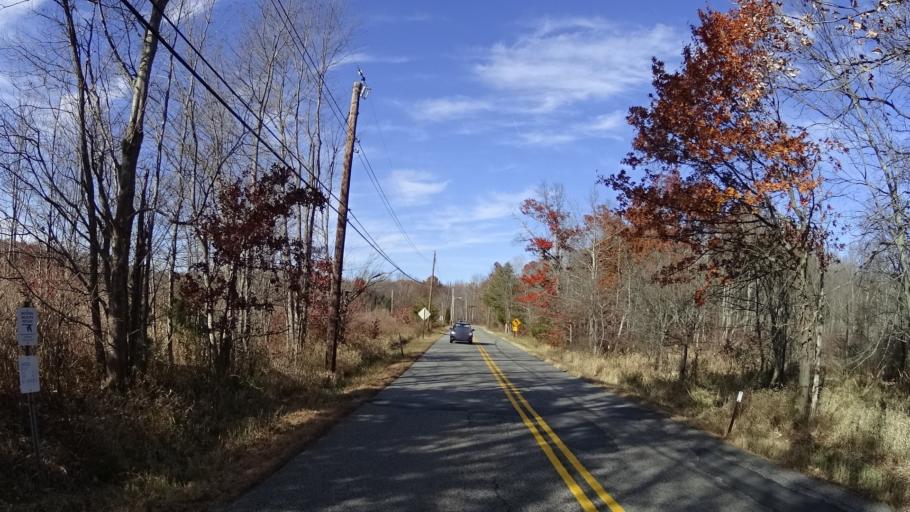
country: US
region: New Jersey
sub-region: Union County
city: Berkeley Heights
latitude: 40.7061
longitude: -74.4761
